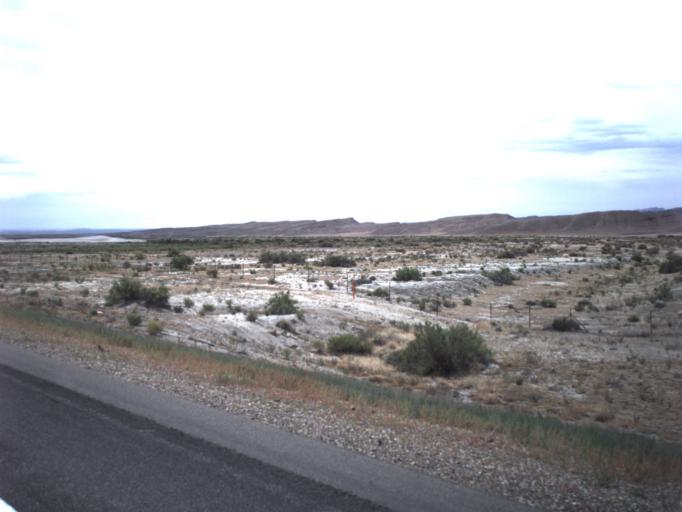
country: US
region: Utah
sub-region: Carbon County
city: East Carbon City
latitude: 39.1257
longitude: -110.3337
